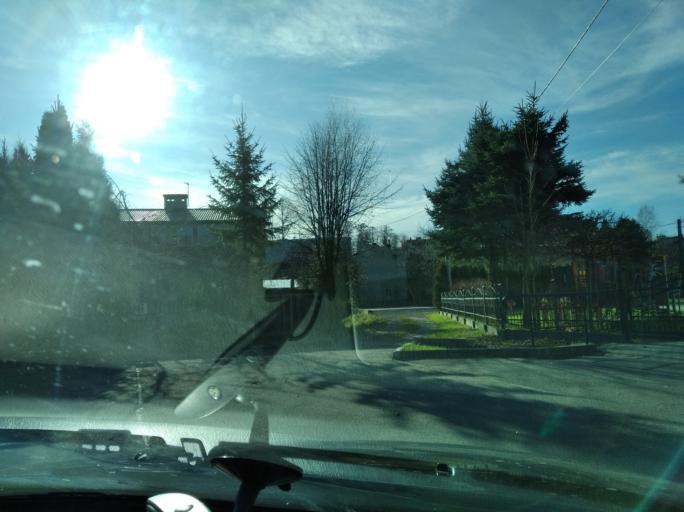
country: PL
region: Subcarpathian Voivodeship
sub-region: Powiat rzeszowski
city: Lutoryz
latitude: 49.9668
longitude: 21.9116
